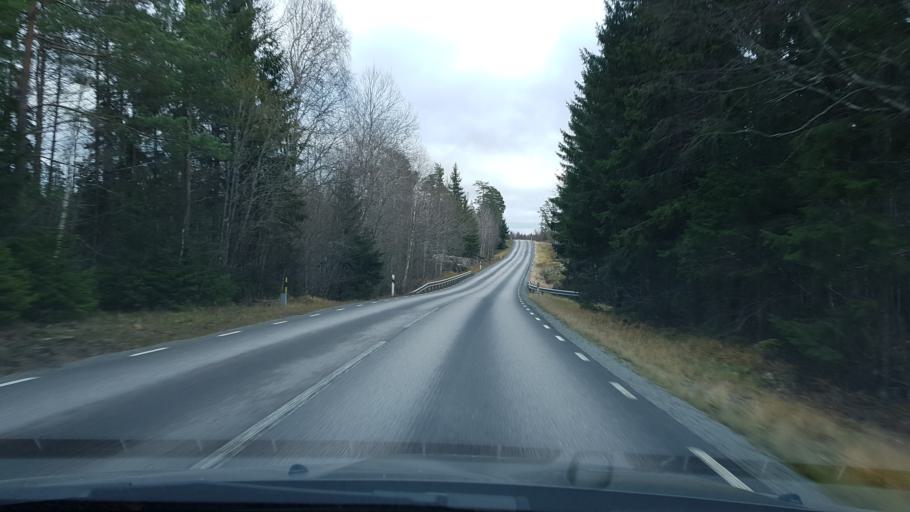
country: SE
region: Stockholm
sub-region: Norrtalje Kommun
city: Skanninge
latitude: 60.0342
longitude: 18.4539
